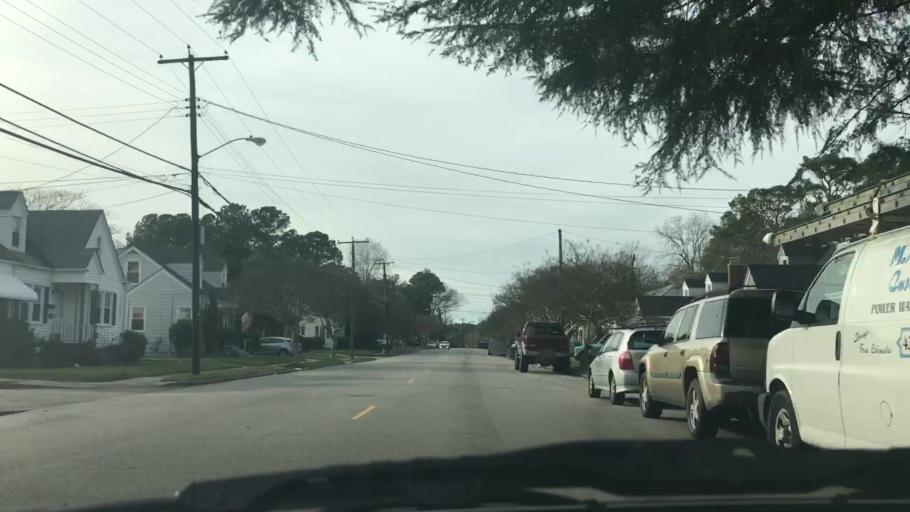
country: US
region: Virginia
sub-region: City of Norfolk
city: Norfolk
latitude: 36.8900
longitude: -76.2492
